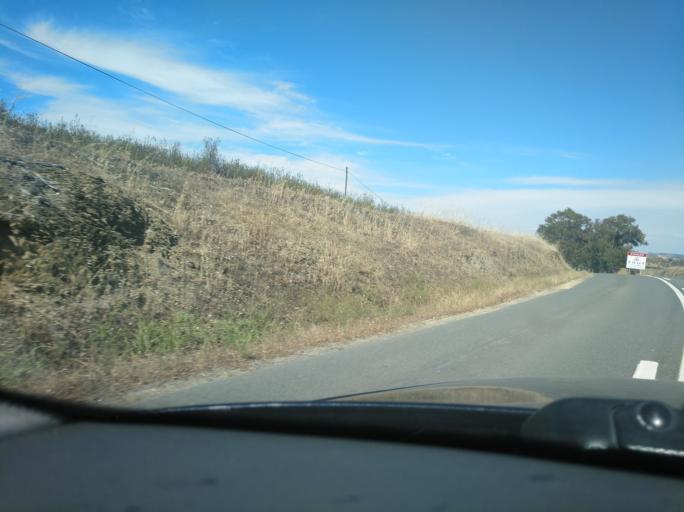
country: PT
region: Beja
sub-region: Mertola
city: Mertola
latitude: 37.6216
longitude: -7.7376
